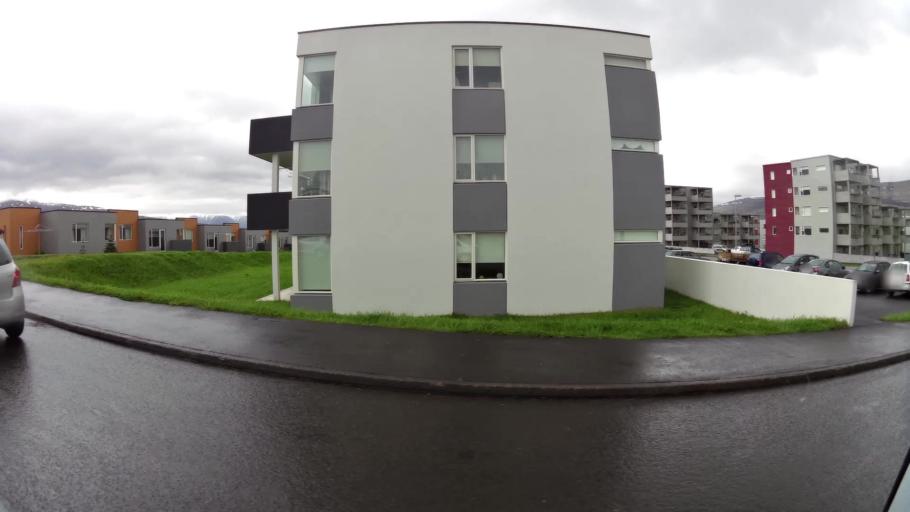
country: IS
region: Northeast
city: Akureyri
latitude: 65.6630
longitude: -18.1000
